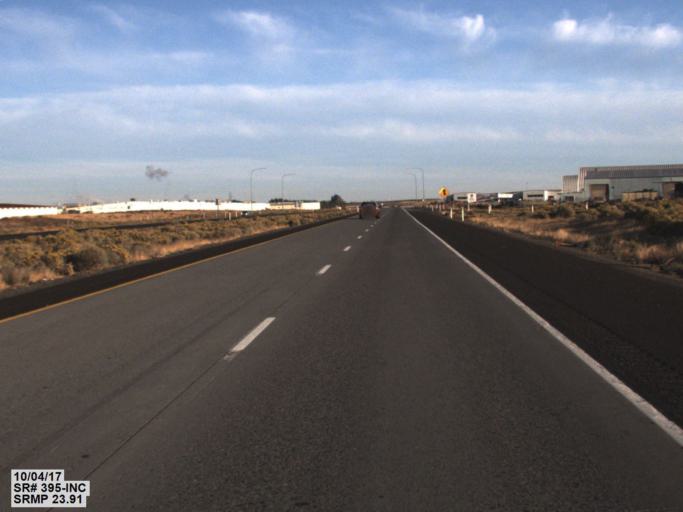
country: US
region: Washington
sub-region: Franklin County
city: Pasco
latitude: 46.2681
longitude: -119.0876
